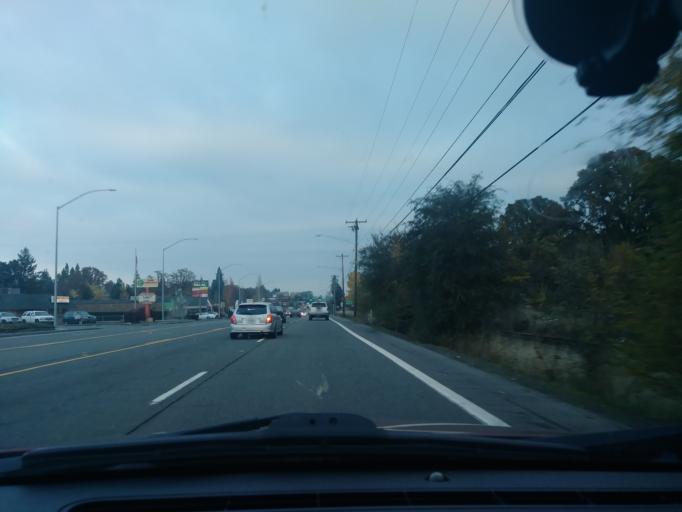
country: US
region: Oregon
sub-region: Washington County
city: Aloha
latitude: 45.4933
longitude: -122.8632
